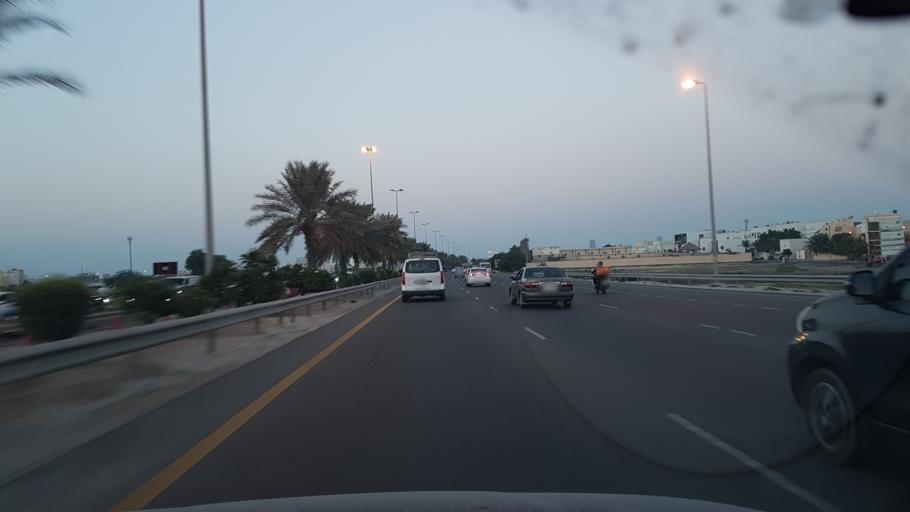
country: BH
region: Northern
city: Madinat `Isa
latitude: 26.1929
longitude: 50.5062
